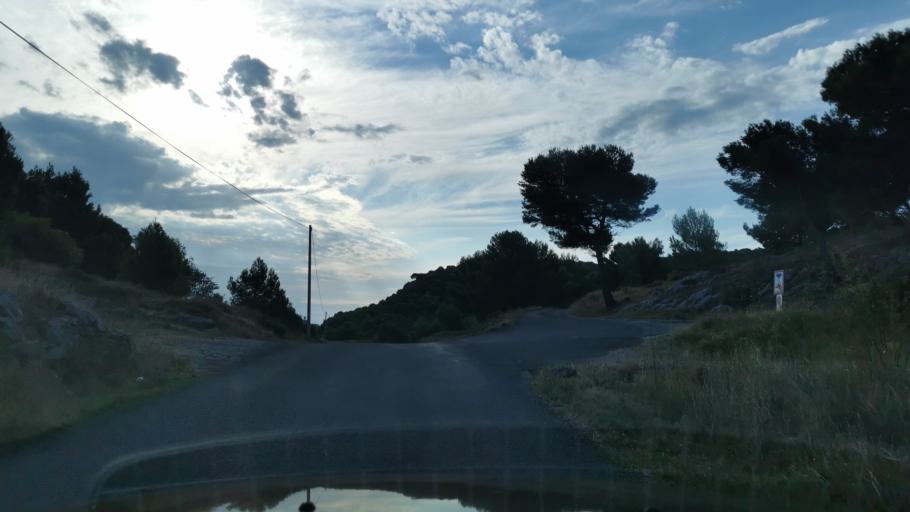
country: FR
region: Languedoc-Roussillon
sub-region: Departement de l'Aude
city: Gruissan
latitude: 43.1079
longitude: 3.0722
